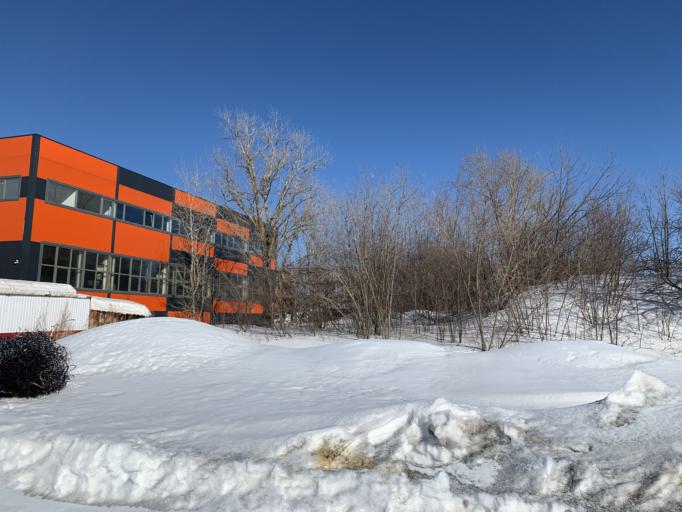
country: RU
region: Chuvashia
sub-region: Cheboksarskiy Rayon
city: Cheboksary
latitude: 56.1408
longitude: 47.2796
